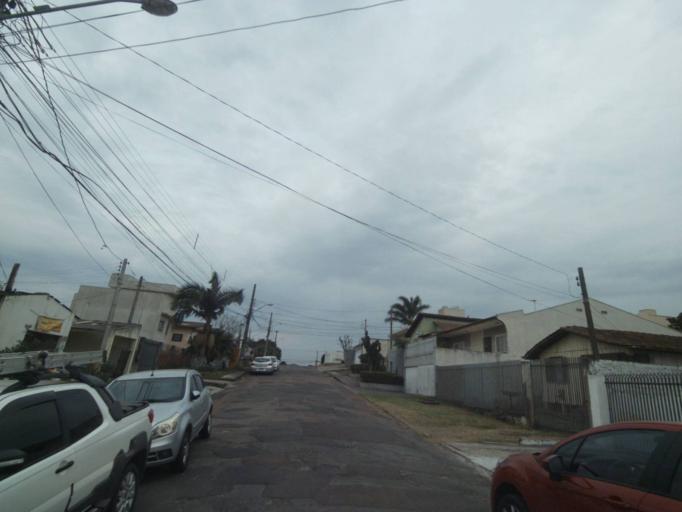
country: BR
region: Parana
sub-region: Pinhais
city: Pinhais
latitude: -25.4793
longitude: -49.2282
